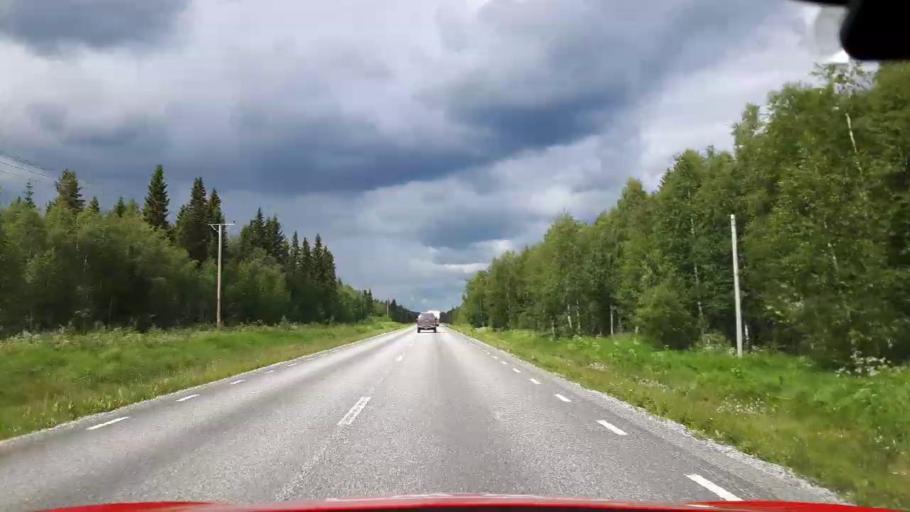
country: SE
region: Jaemtland
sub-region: Krokoms Kommun
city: Krokom
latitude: 63.6615
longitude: 14.3617
